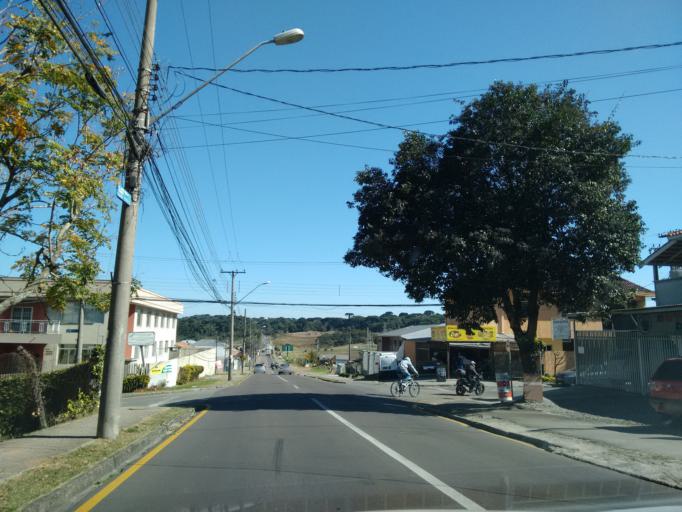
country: BR
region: Parana
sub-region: Curitiba
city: Curitiba
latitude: -25.5121
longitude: -49.3061
